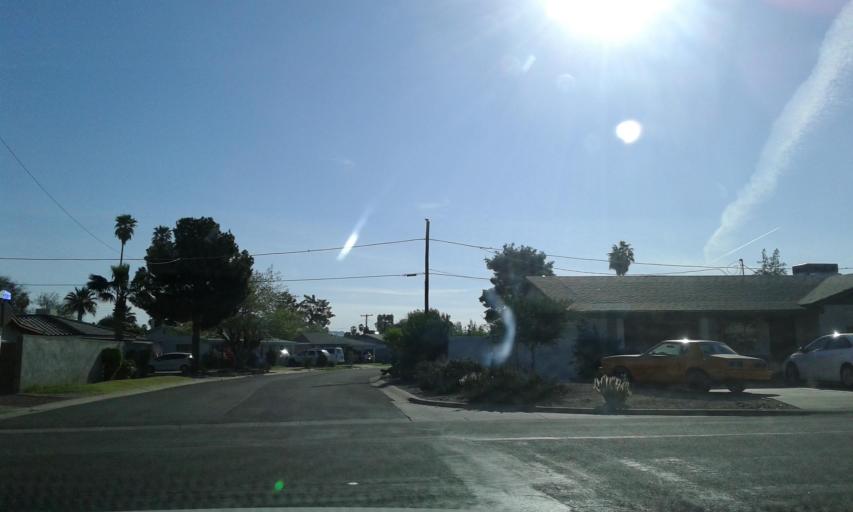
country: US
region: Arizona
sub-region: Maricopa County
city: Glendale
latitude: 33.5399
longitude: -112.1069
